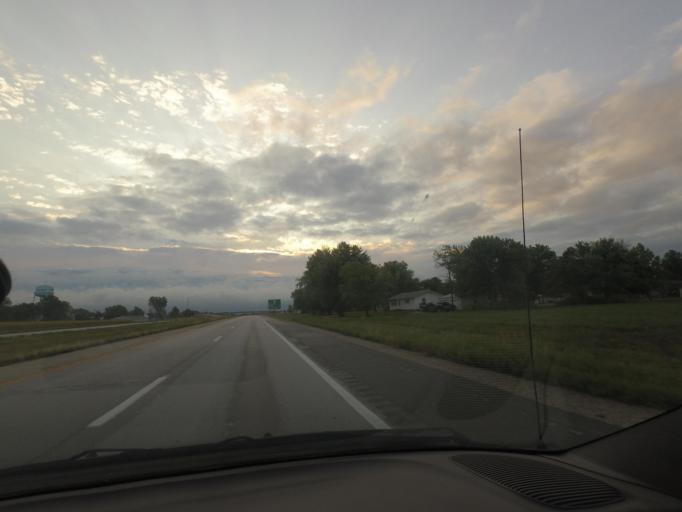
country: US
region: Missouri
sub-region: Shelby County
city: Shelbina
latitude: 39.6979
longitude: -92.0473
